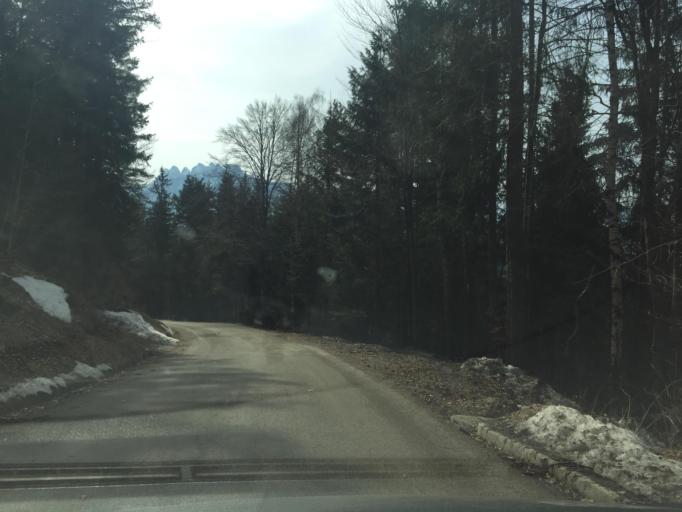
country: IT
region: Friuli Venezia Giulia
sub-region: Provincia di Udine
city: Tarvisio
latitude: 46.5058
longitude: 13.6385
